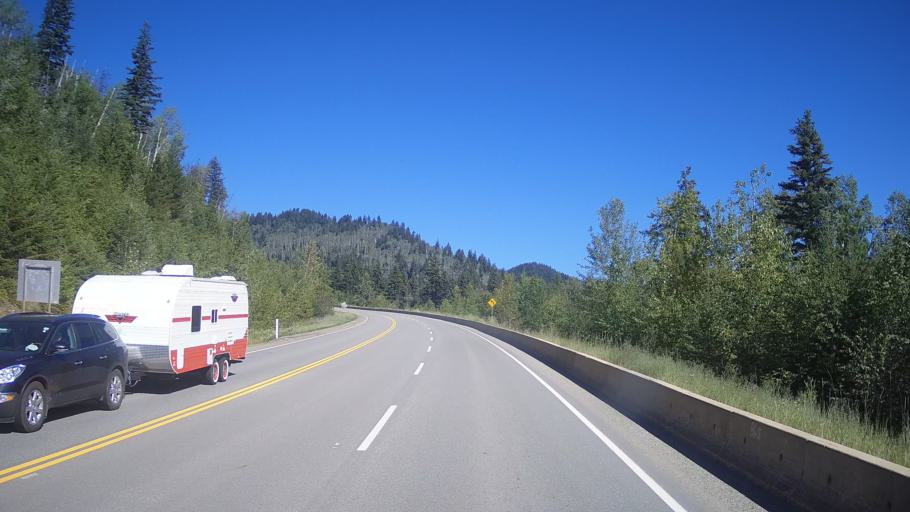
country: CA
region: British Columbia
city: Kamloops
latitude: 51.4931
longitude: -120.2707
